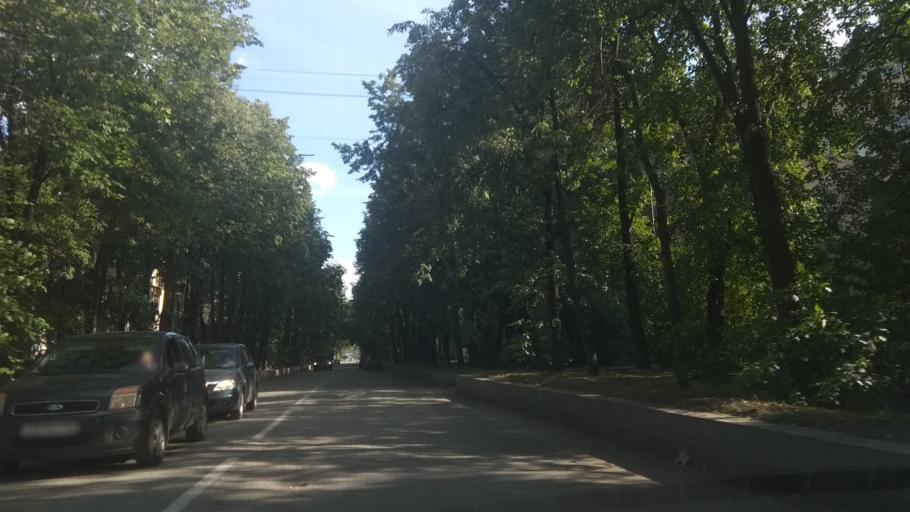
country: RU
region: Sverdlovsk
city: Yekaterinburg
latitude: 56.8996
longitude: 60.5886
